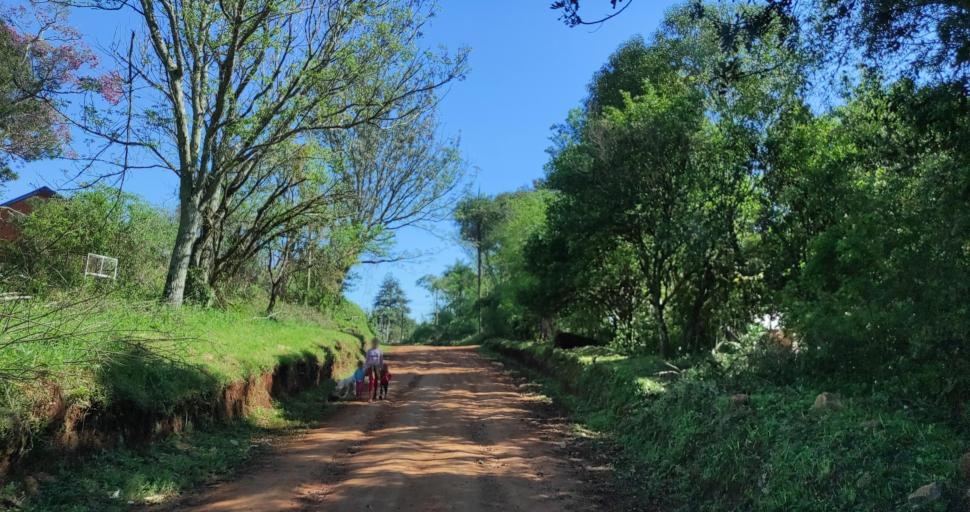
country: AR
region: Misiones
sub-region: Departamento de Candelaria
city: Loreto
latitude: -27.3114
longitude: -55.5376
